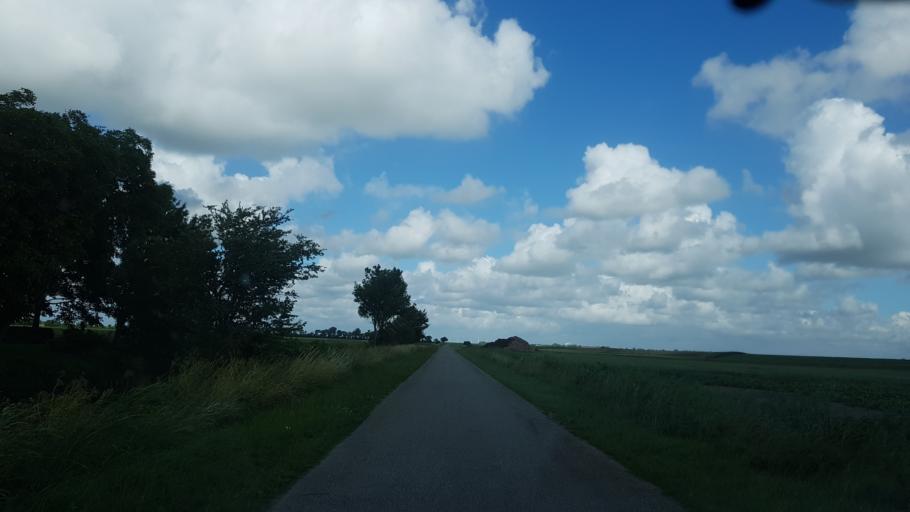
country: NL
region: Groningen
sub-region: Gemeente Bedum
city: Bedum
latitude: 53.4225
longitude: 6.6303
